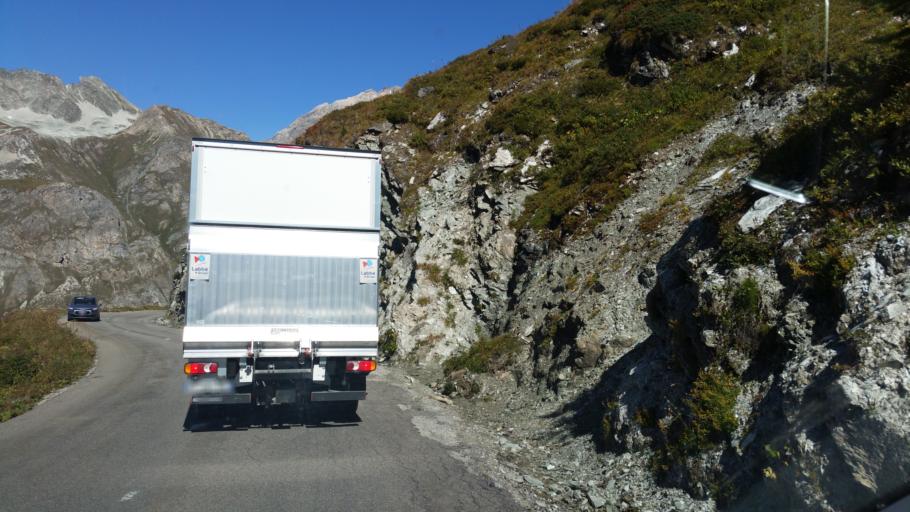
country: FR
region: Rhone-Alpes
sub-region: Departement de la Savoie
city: Val-d'Isere
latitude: 45.4369
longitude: 7.0041
